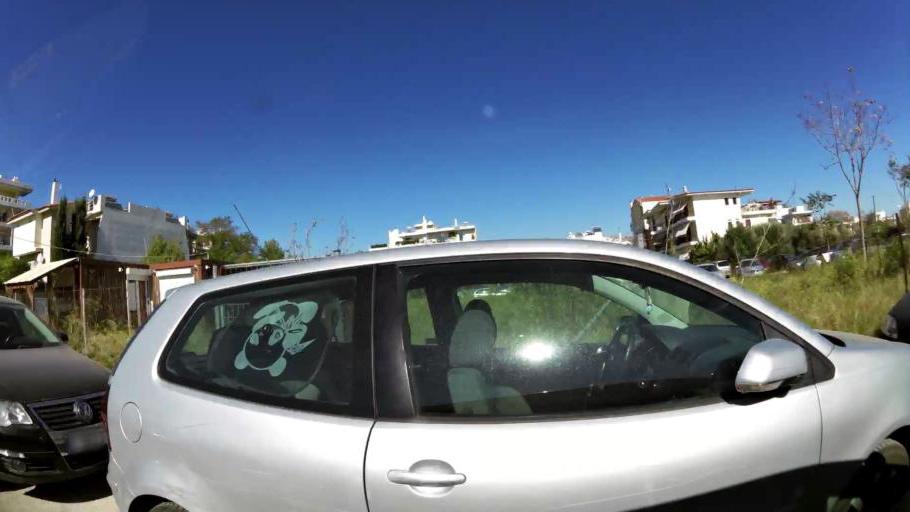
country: GR
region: Attica
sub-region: Nomarchia Athinas
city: Agia Paraskevi
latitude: 38.0223
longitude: 23.8190
